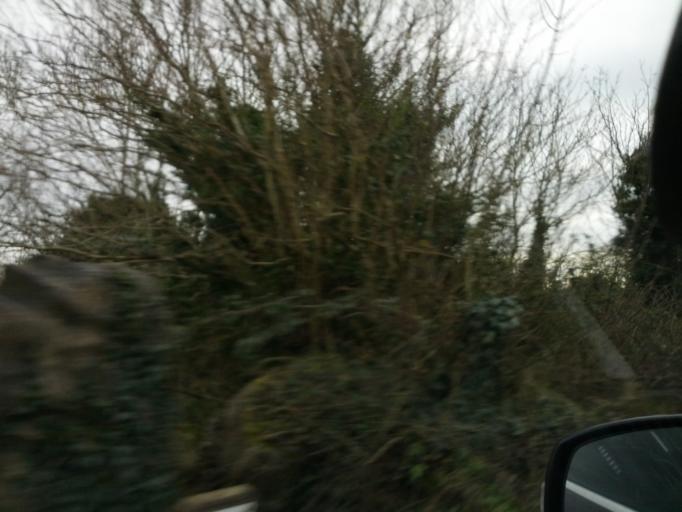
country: IE
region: Connaught
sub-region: County Galway
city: Athenry
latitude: 53.2301
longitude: -8.7858
